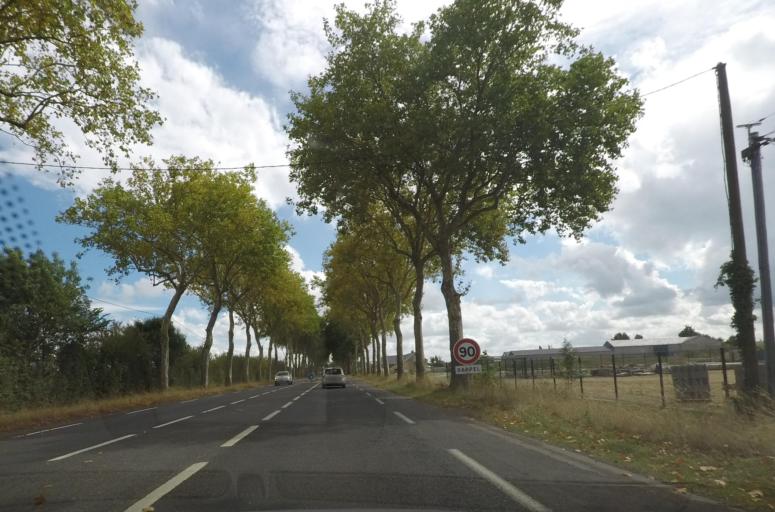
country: FR
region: Pays de la Loire
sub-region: Departement de la Sarthe
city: La Fleche
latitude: 47.6953
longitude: -0.1025
